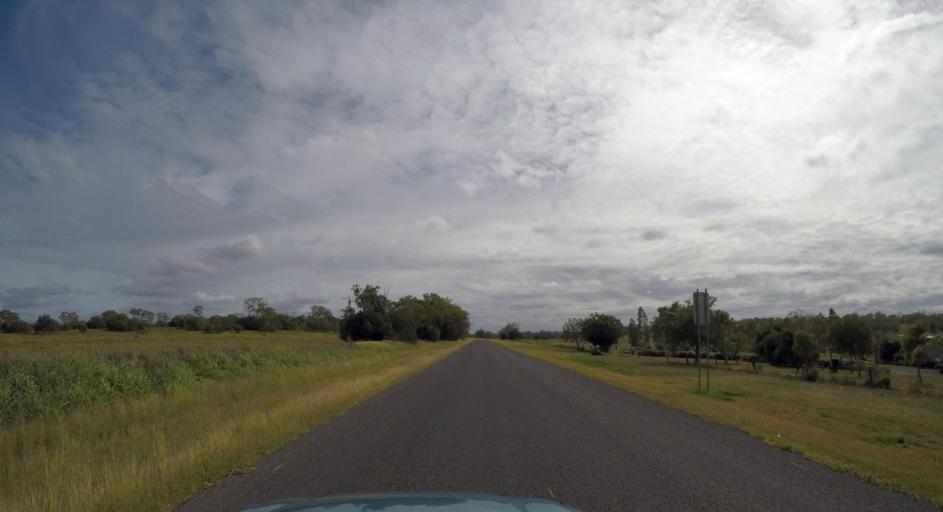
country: AU
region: Queensland
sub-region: Western Downs
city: Dalby
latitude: -27.0452
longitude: 151.3103
